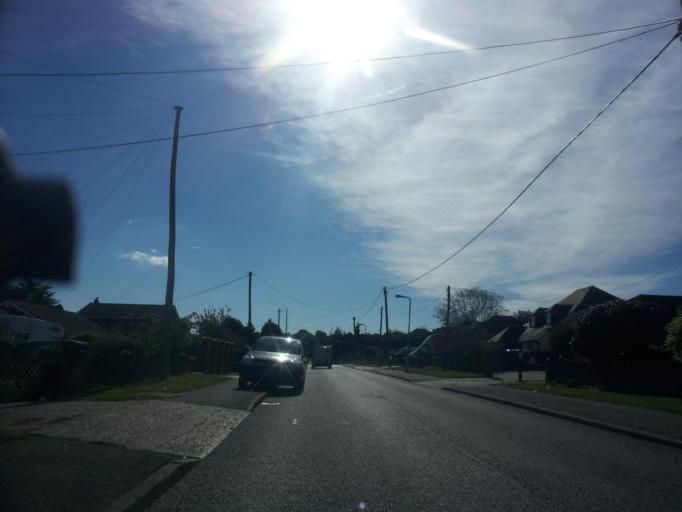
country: GB
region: England
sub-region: Kent
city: Chatham
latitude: 51.3387
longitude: 0.5205
